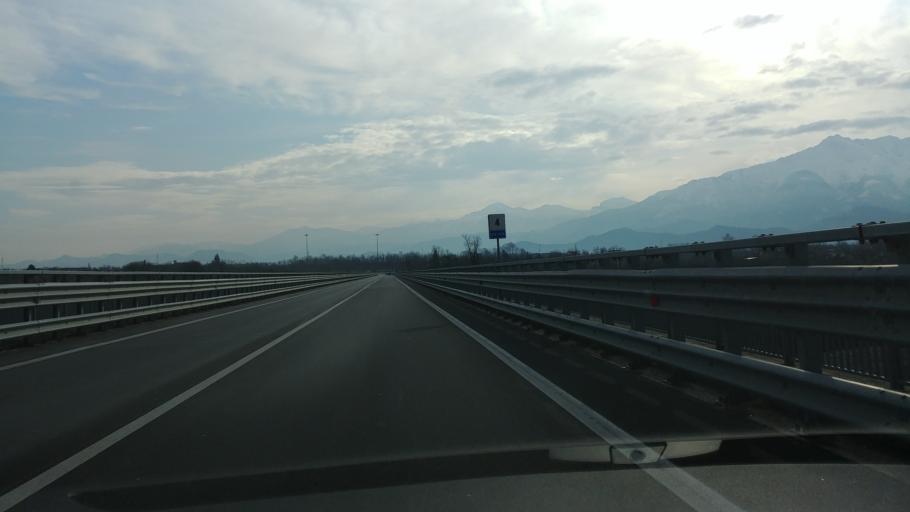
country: IT
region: Piedmont
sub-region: Provincia di Cuneo
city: Cuneo
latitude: 44.3714
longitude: 7.5458
